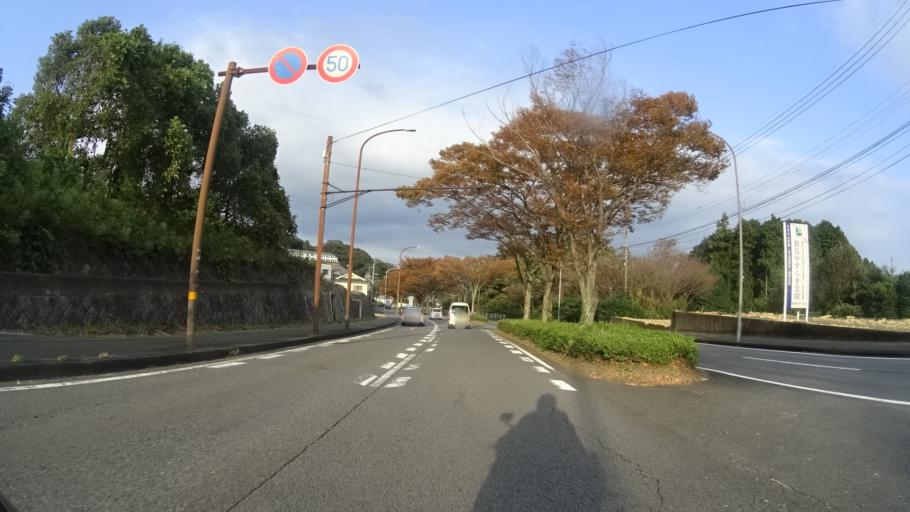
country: JP
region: Oita
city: Beppu
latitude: 33.3137
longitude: 131.4693
